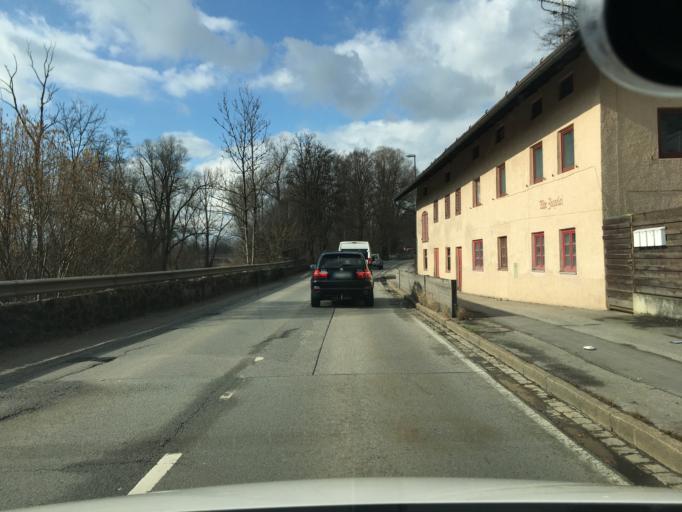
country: DE
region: Bavaria
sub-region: Upper Bavaria
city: Rosenheim
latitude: 47.8503
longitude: 12.1518
